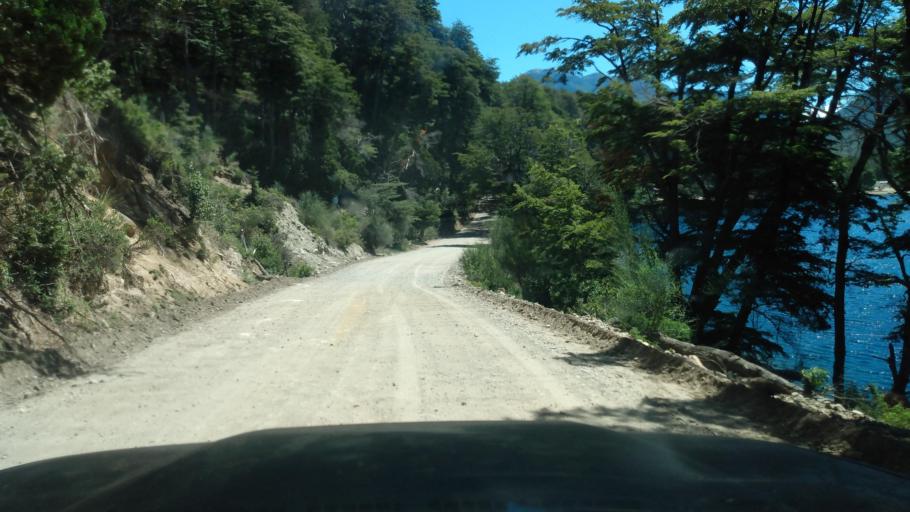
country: AR
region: Neuquen
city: Villa La Angostura
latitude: -40.6162
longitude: -71.5422
